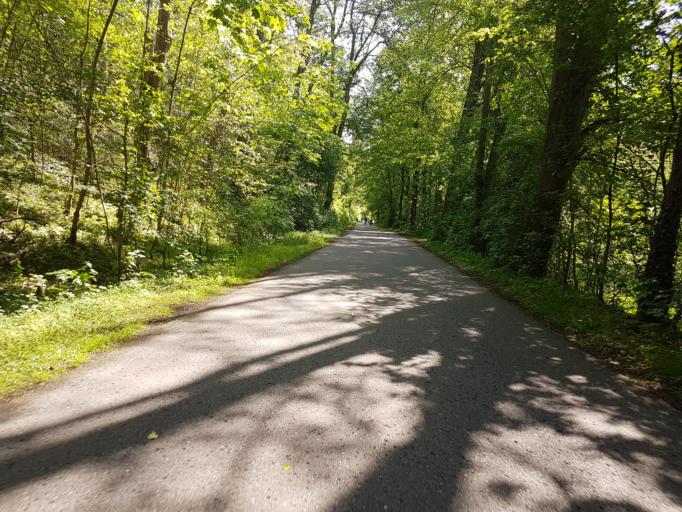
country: DE
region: Baden-Wuerttemberg
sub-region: Regierungsbezirk Stuttgart
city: Besigheim
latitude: 48.9701
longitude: 9.1475
